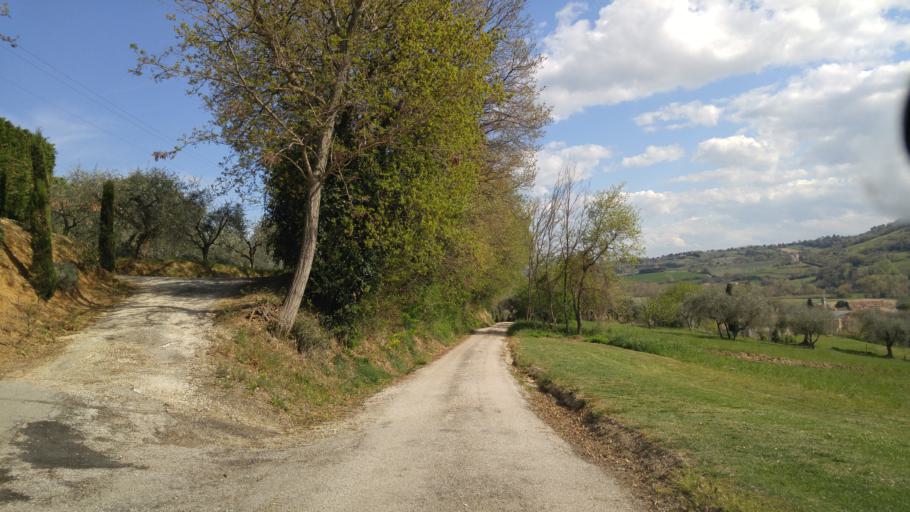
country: IT
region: The Marches
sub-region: Provincia di Pesaro e Urbino
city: Fenile
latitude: 43.8452
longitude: 12.9627
